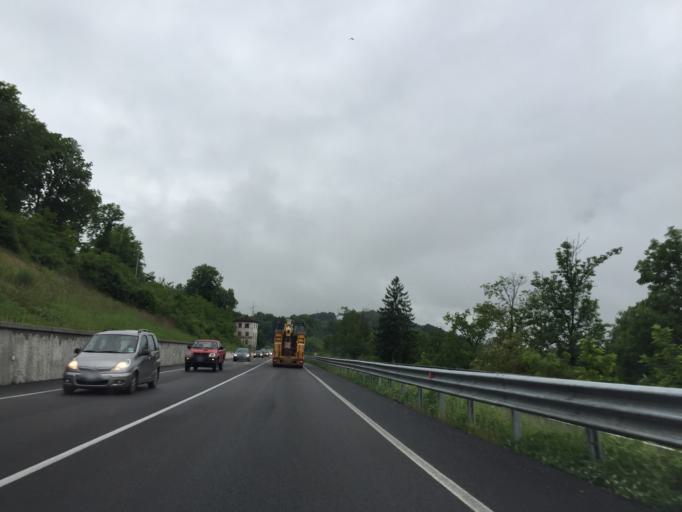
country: IT
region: Veneto
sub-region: Provincia di Belluno
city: Castion
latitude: 46.1381
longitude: 12.2325
